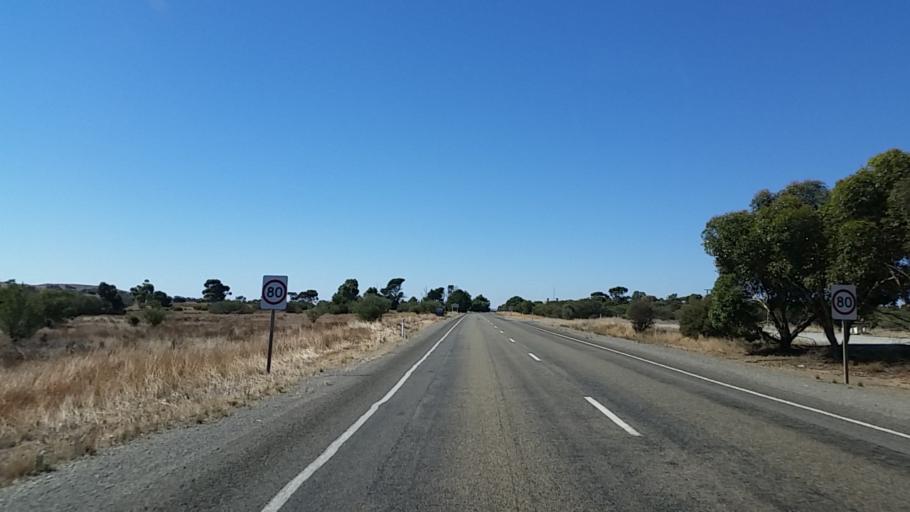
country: AU
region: South Australia
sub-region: Peterborough
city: Peterborough
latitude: -33.2315
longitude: 138.8806
